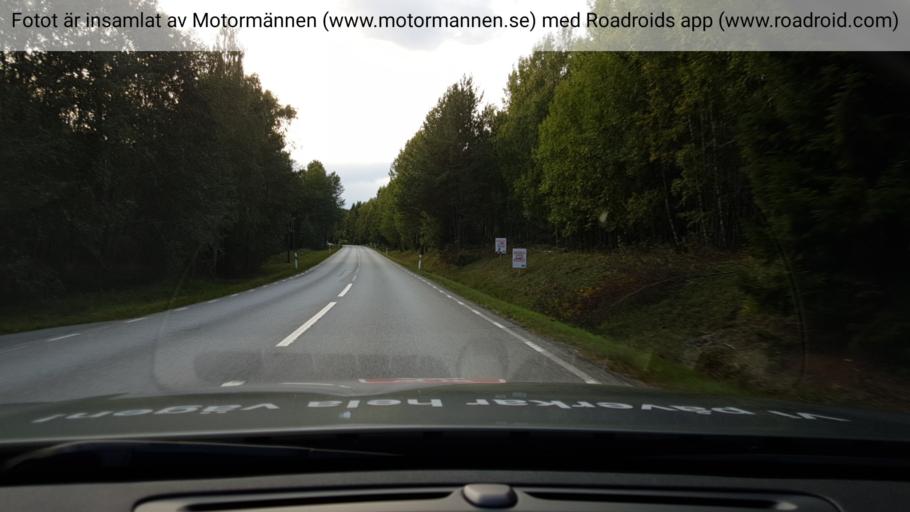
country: SE
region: OErebro
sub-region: Ljusnarsbergs Kommun
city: Kopparberg
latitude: 59.7876
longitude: 14.7707
